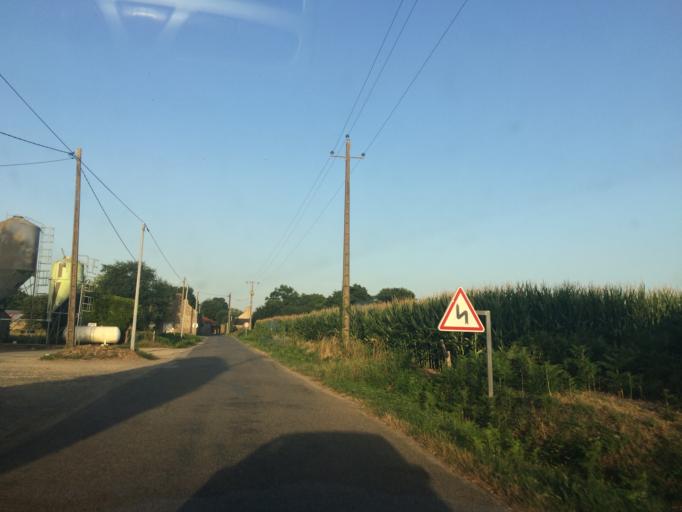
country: FR
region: Brittany
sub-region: Departement du Morbihan
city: Beganne
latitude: 47.6361
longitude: -2.2426
